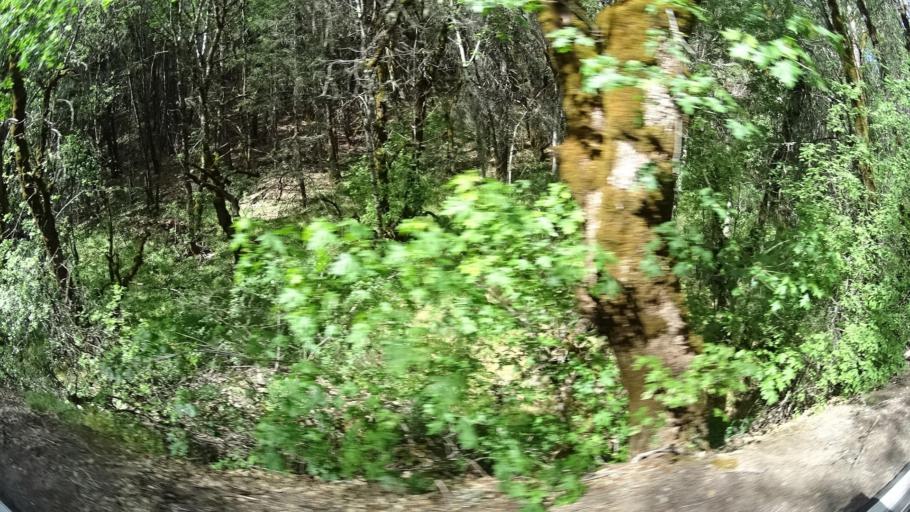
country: US
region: California
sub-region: Lake County
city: Cobb
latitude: 38.8949
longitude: -122.7378
